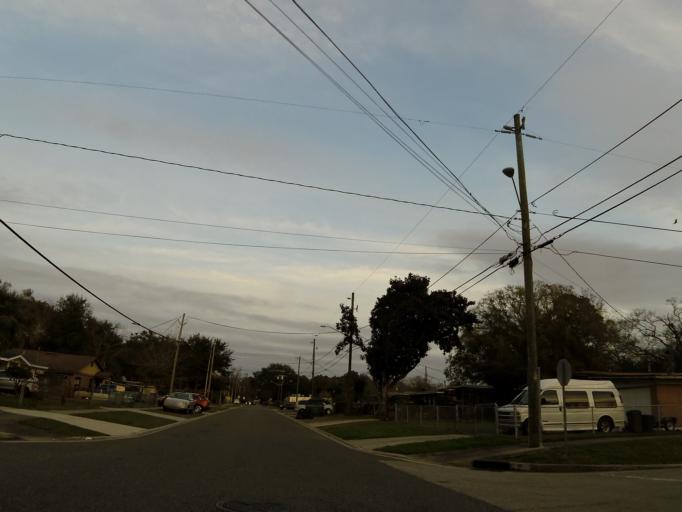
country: US
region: Florida
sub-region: Duval County
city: Jacksonville
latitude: 30.3580
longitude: -81.7035
